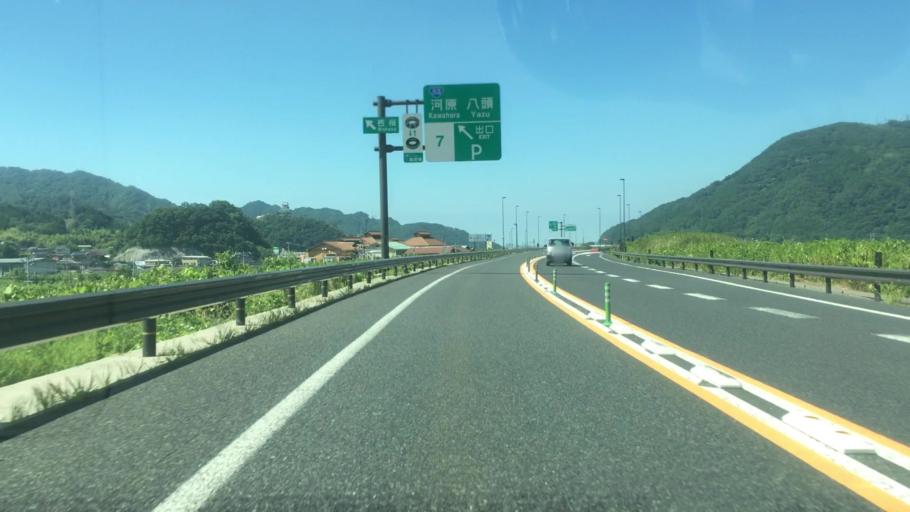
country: JP
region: Tottori
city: Tottori
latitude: 35.3905
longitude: 134.2033
